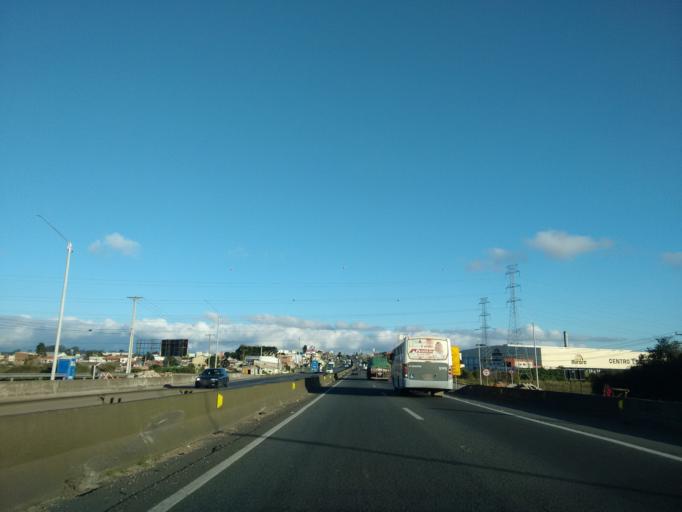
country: BR
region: Parana
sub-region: Sao Jose Dos Pinhais
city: Sao Jose dos Pinhais
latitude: -25.5987
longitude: -49.1737
